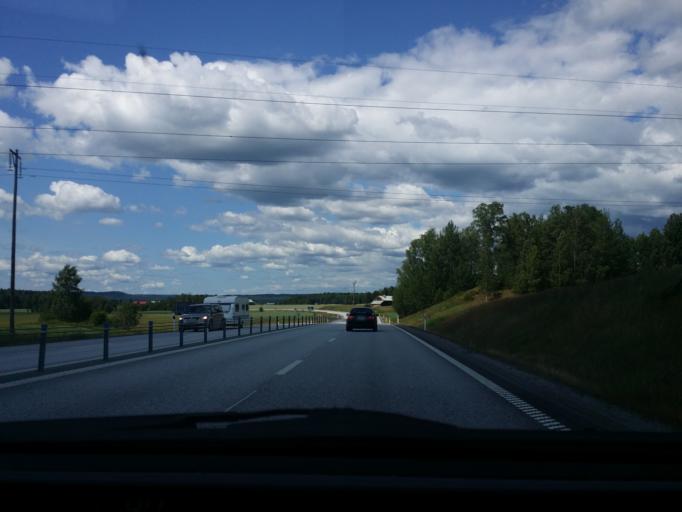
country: SE
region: OErebro
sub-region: Orebro Kommun
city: Hovsta
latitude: 59.3947
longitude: 15.2056
